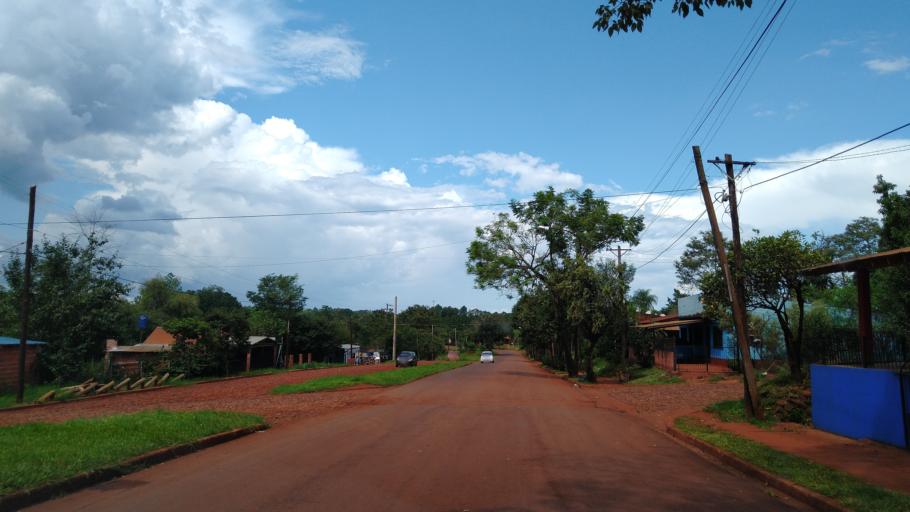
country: AR
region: Misiones
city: Puerto Libertad
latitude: -25.9670
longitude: -54.5900
